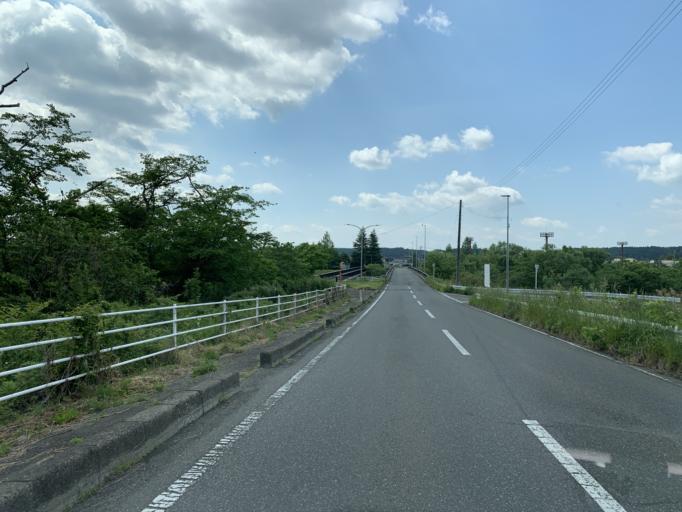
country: JP
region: Miyagi
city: Furukawa
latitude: 38.7476
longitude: 140.9536
